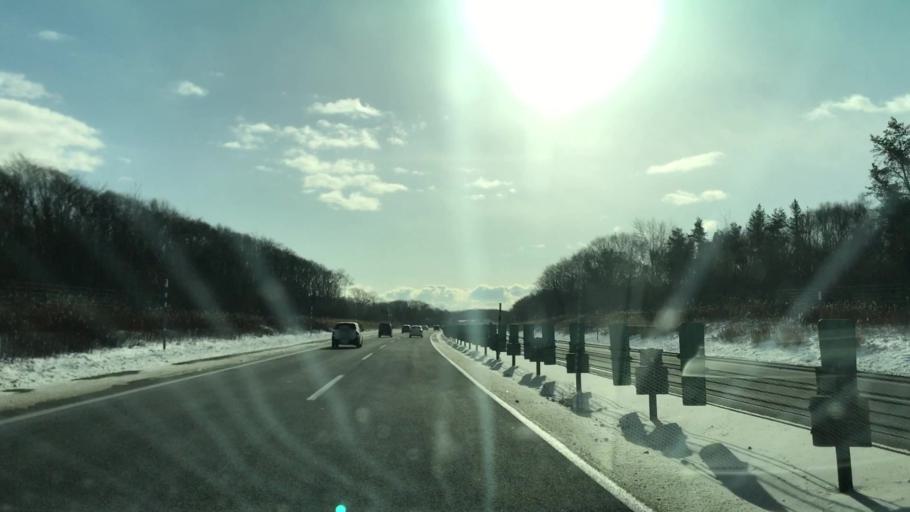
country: JP
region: Hokkaido
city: Chitose
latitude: 42.8328
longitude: 141.6101
